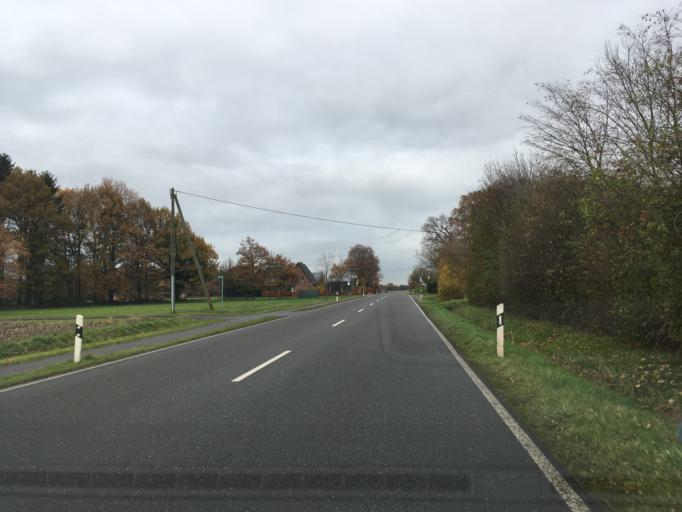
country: DE
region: North Rhine-Westphalia
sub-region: Regierungsbezirk Munster
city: Gescher
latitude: 51.9797
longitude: 7.0249
